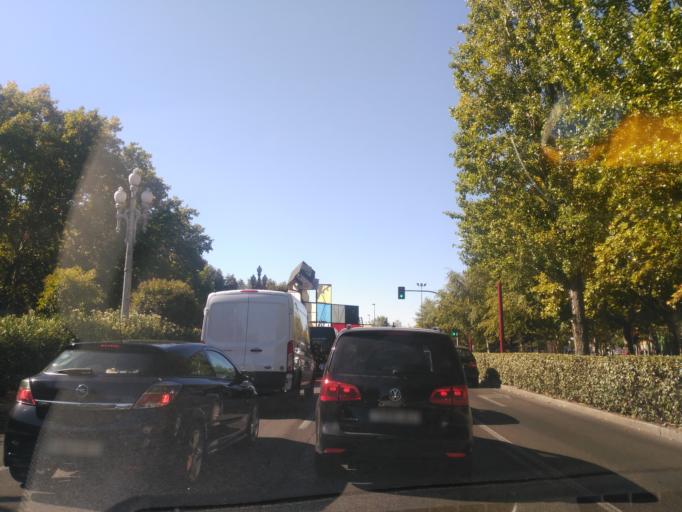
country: ES
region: Castille and Leon
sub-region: Provincia de Valladolid
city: Valladolid
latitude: 41.6288
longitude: -4.7430
